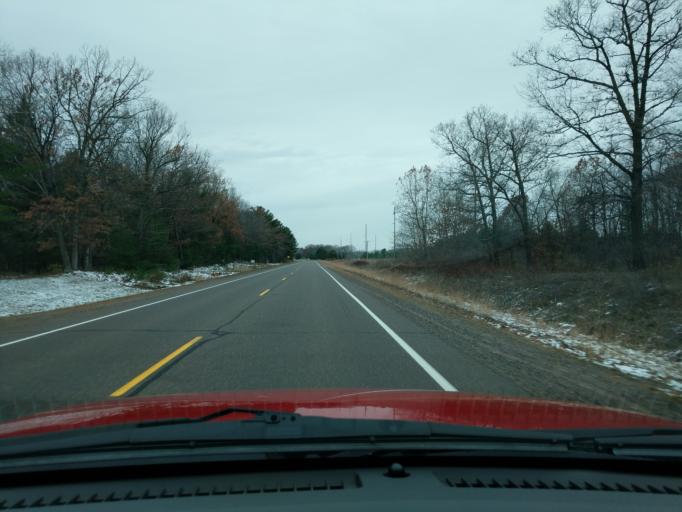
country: US
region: Wisconsin
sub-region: Burnett County
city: Siren
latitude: 45.8215
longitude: -92.2474
